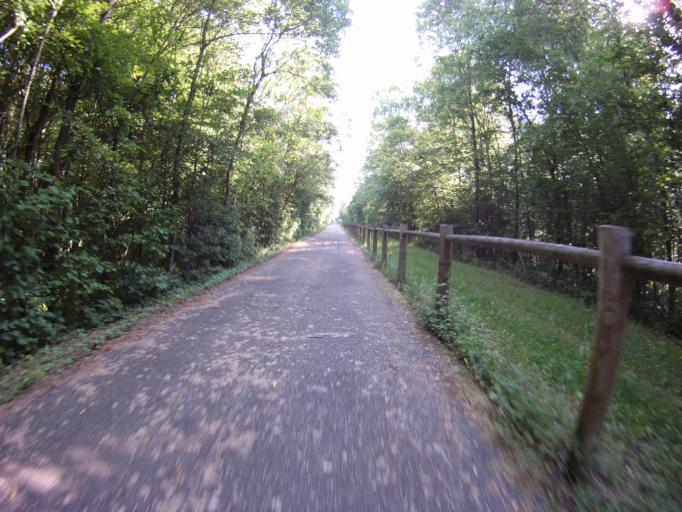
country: FR
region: Lorraine
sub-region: Departement de Meurthe-et-Moselle
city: Champenoux
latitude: 48.7428
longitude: 6.3174
